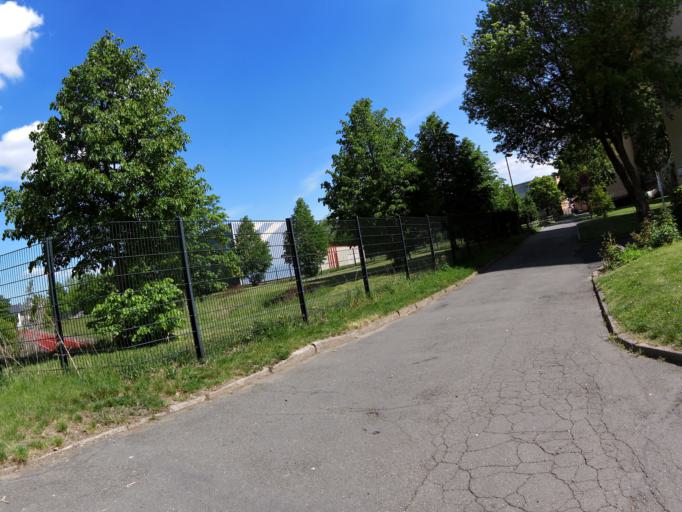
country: DE
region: Thuringia
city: Bad Salzungen
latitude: 50.8089
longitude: 10.2178
